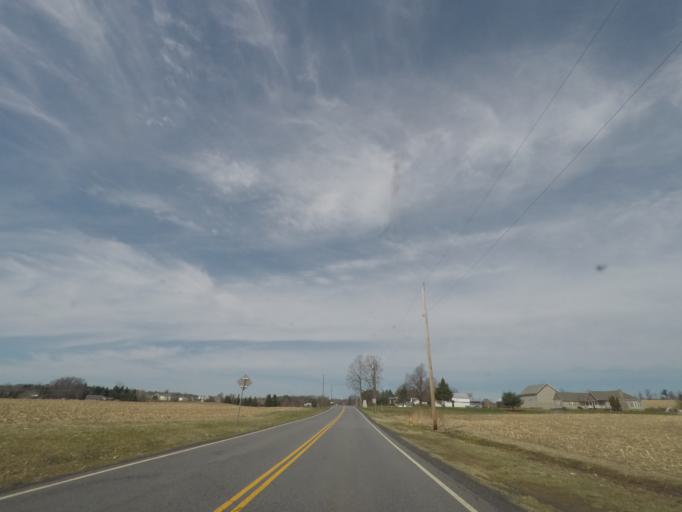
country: US
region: New York
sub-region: Saratoga County
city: Mechanicville
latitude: 42.9022
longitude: -73.7394
